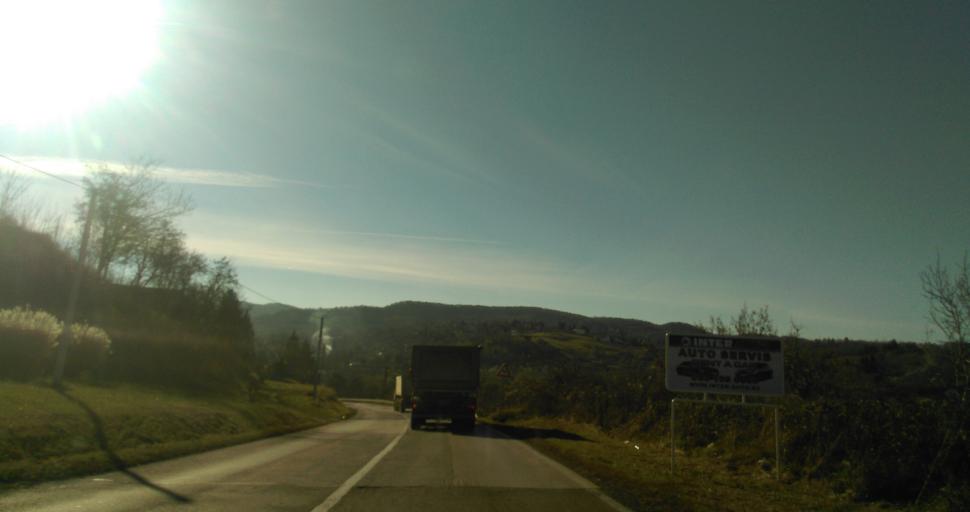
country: RS
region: Autonomna Pokrajina Vojvodina
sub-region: Juznobacki Okrug
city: Novi Sad
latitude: 45.2050
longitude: 19.8430
